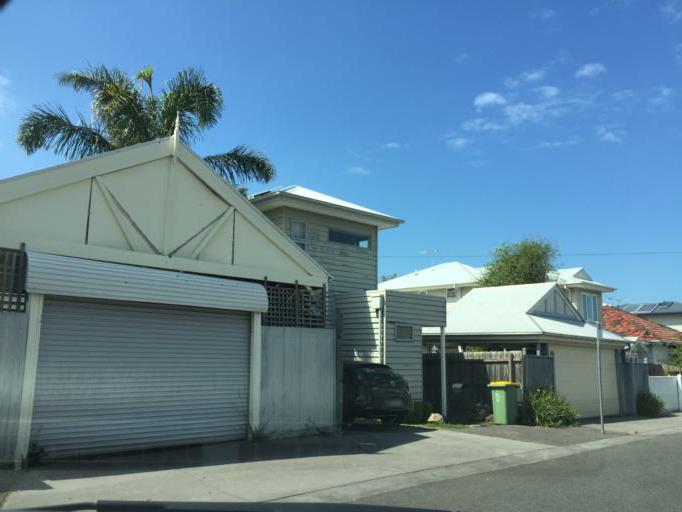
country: AU
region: Victoria
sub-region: Maribyrnong
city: West Footscray
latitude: -37.7943
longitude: 144.8871
